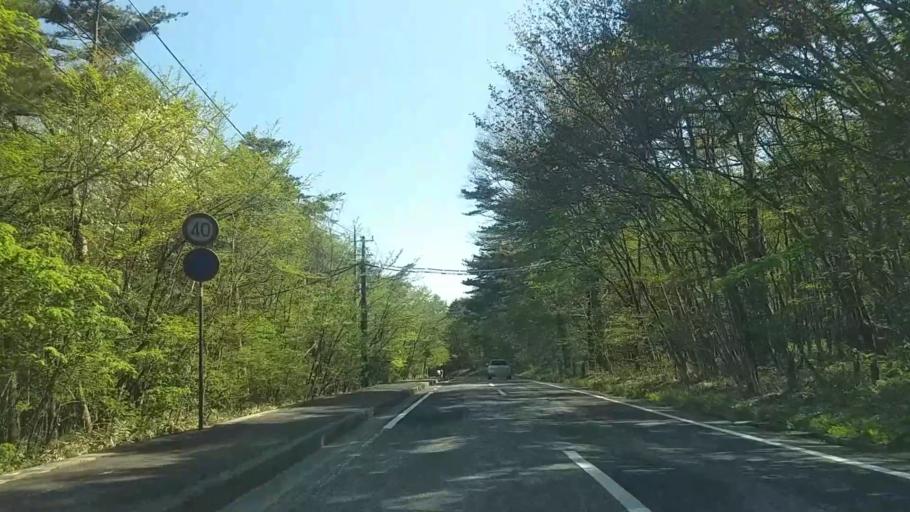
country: JP
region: Yamanashi
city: Nirasaki
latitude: 35.9289
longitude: 138.4191
